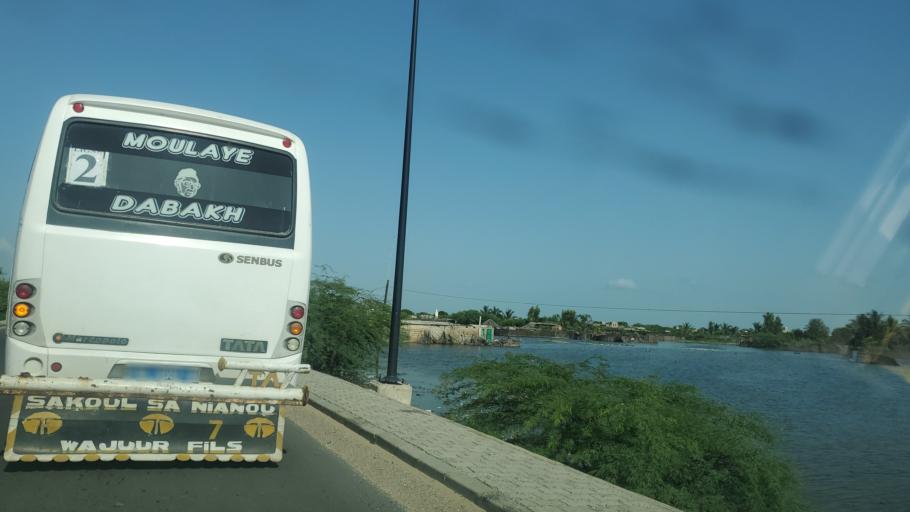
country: SN
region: Saint-Louis
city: Saint-Louis
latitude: 16.0366
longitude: -16.4656
